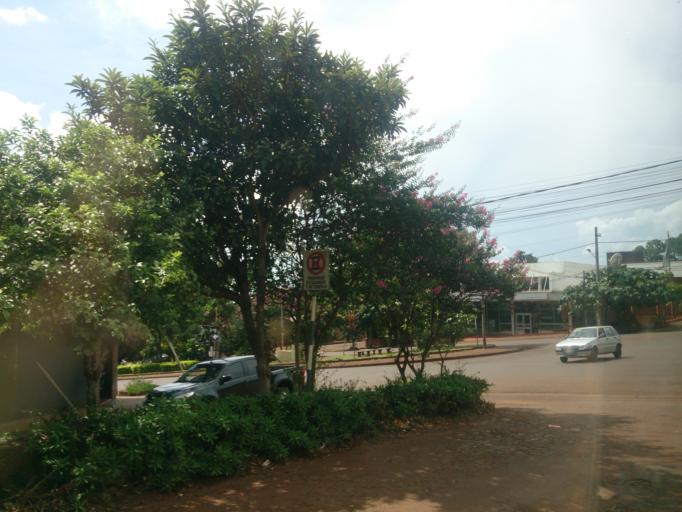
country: AR
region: Misiones
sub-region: Departamento de Obera
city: Obera
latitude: -27.4880
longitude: -55.1129
